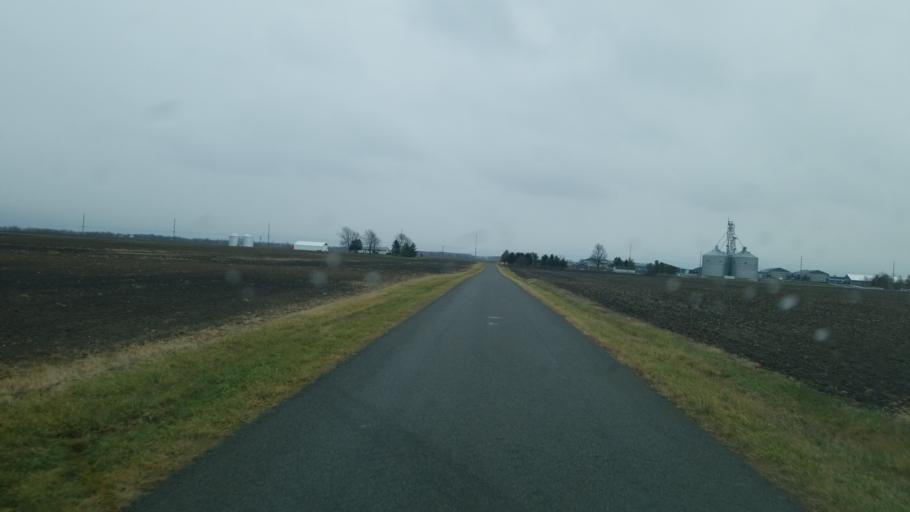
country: US
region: Ohio
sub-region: Logan County
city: Northwood
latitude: 40.4381
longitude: -83.5642
